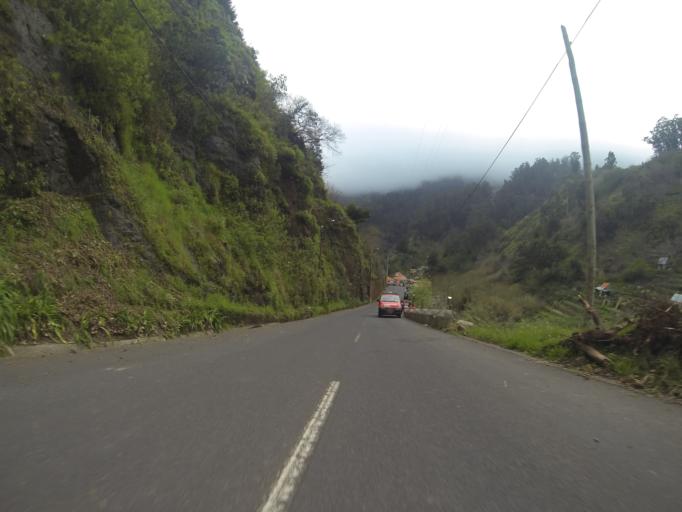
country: PT
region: Madeira
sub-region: Camara de Lobos
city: Curral das Freiras
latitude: 32.7376
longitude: -16.9684
